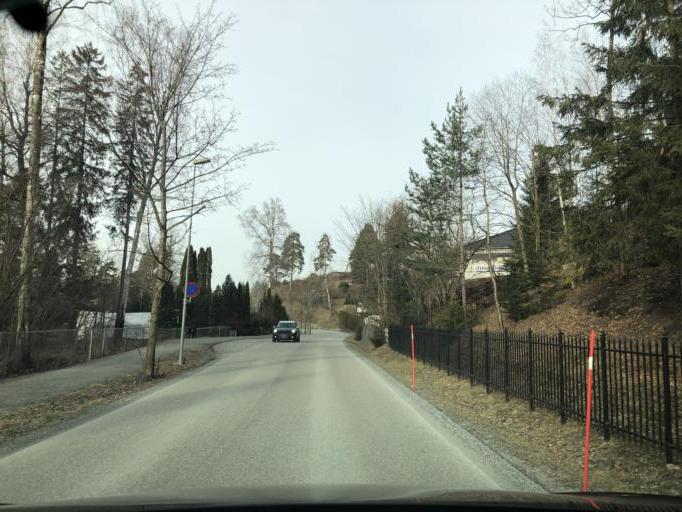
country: NO
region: Akershus
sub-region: Baerum
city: Sandvika
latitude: 59.8625
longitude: 10.5146
